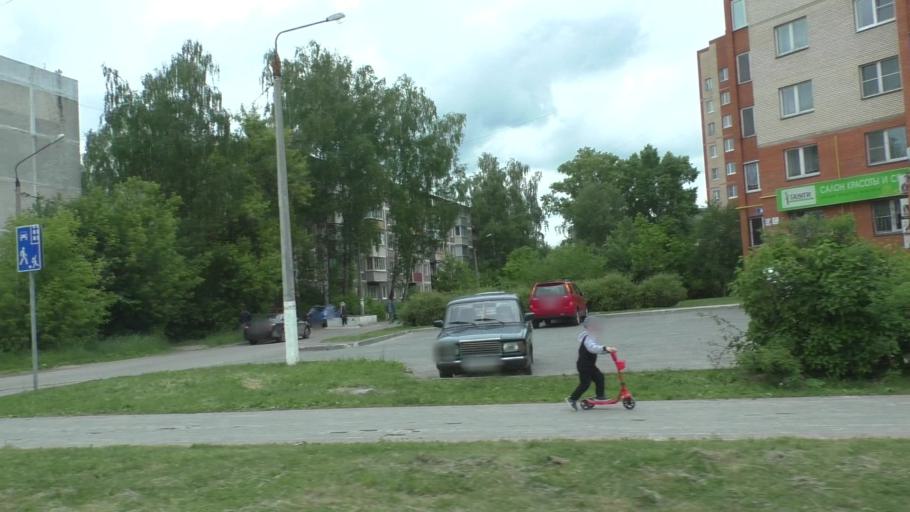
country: RU
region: Moskovskaya
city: Yegor'yevsk
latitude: 55.3680
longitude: 39.0551
